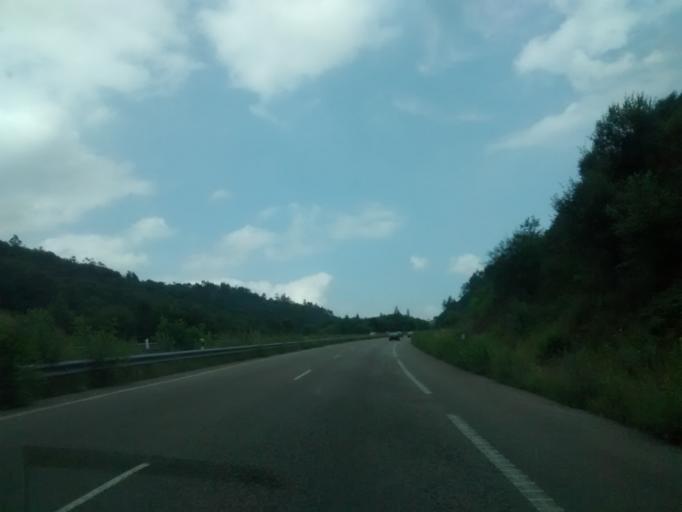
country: ES
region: Asturias
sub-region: Province of Asturias
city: Mieres
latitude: 43.2727
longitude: -5.7720
